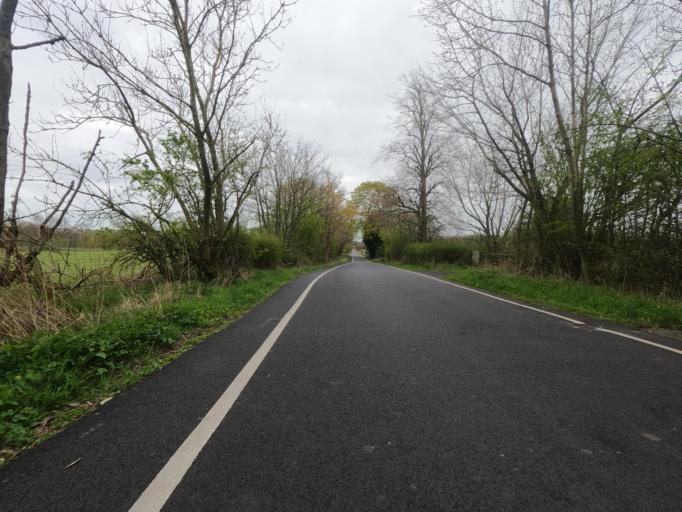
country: GB
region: England
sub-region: Newcastle upon Tyne
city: Dinnington
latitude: 55.0604
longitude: -1.6835
